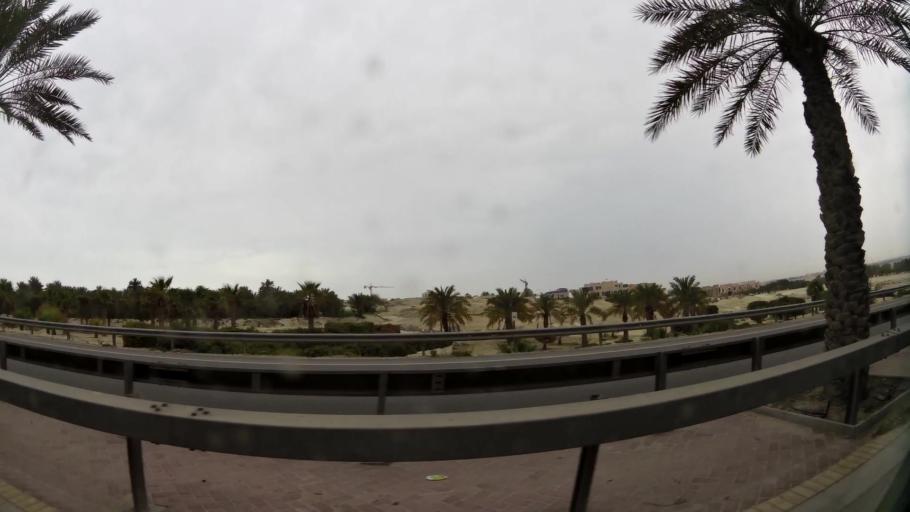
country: BH
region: Northern
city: Ar Rifa'
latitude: 26.1167
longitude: 50.5372
